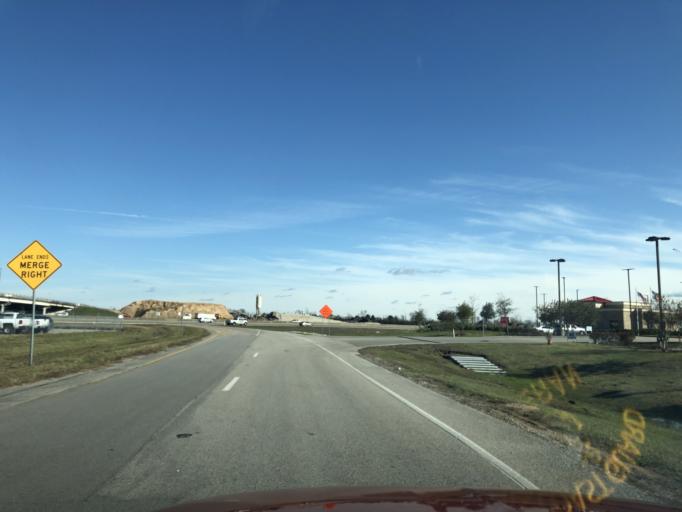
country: US
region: Texas
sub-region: Galveston County
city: Dickinson
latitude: 29.4296
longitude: -95.0618
